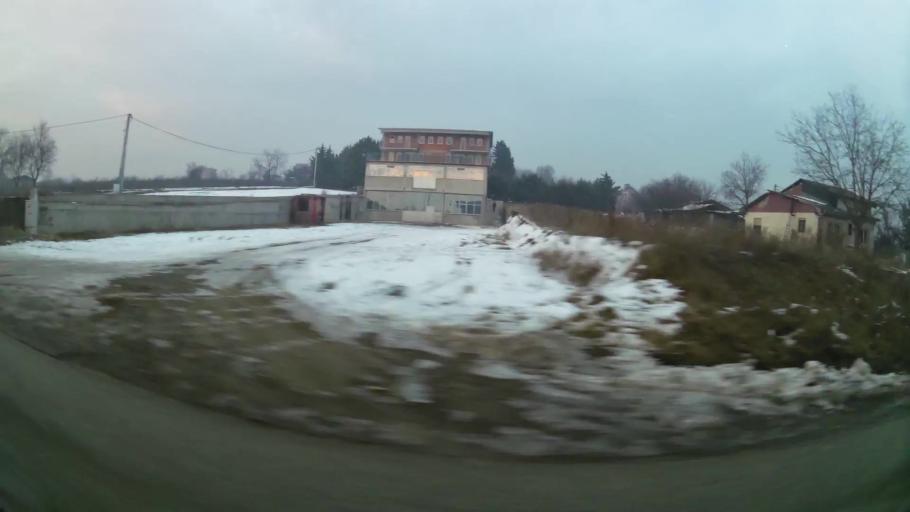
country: MK
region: Suto Orizari
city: Suto Orizare
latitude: 42.0291
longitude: 21.4079
